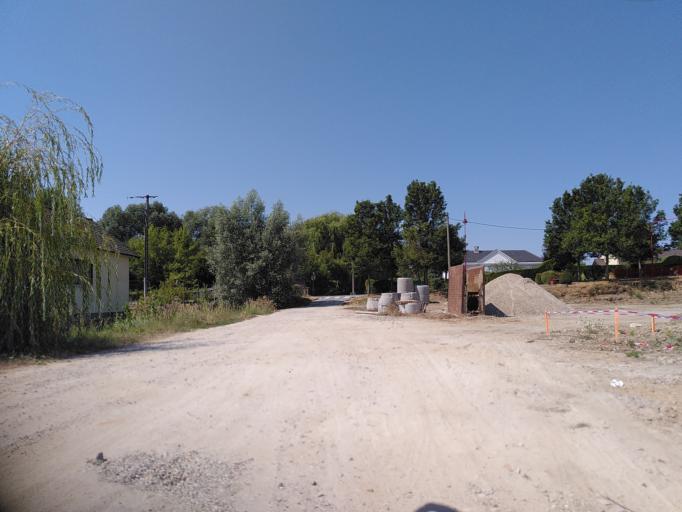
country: FR
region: Ile-de-France
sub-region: Departement de l'Essonne
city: Ollainville
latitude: 48.5861
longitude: 2.2221
